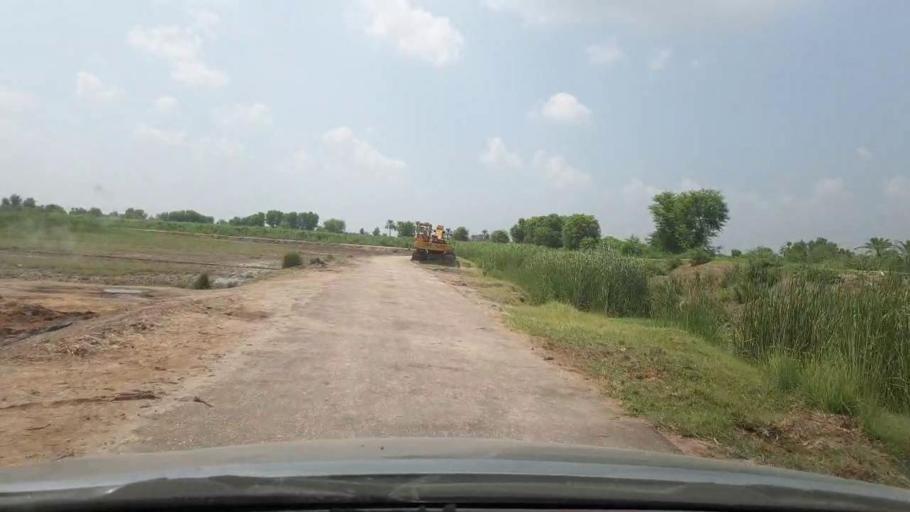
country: PK
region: Sindh
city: Kot Diji
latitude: 27.3947
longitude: 68.7258
